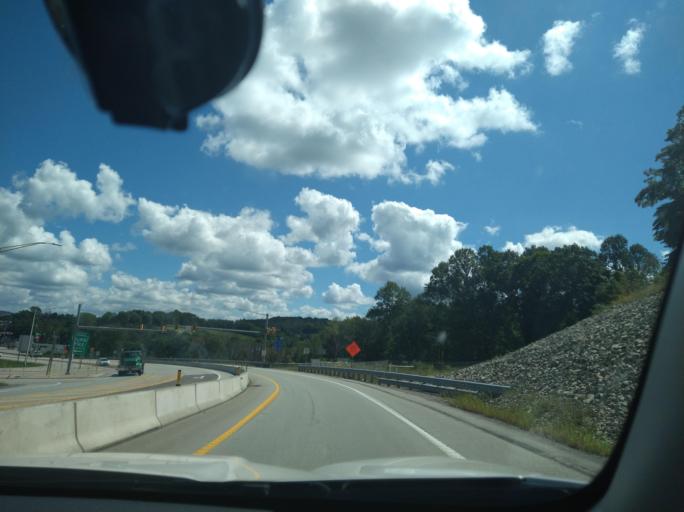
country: US
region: Pennsylvania
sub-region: Fayette County
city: Bear Rocks
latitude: 40.1077
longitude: -79.3831
